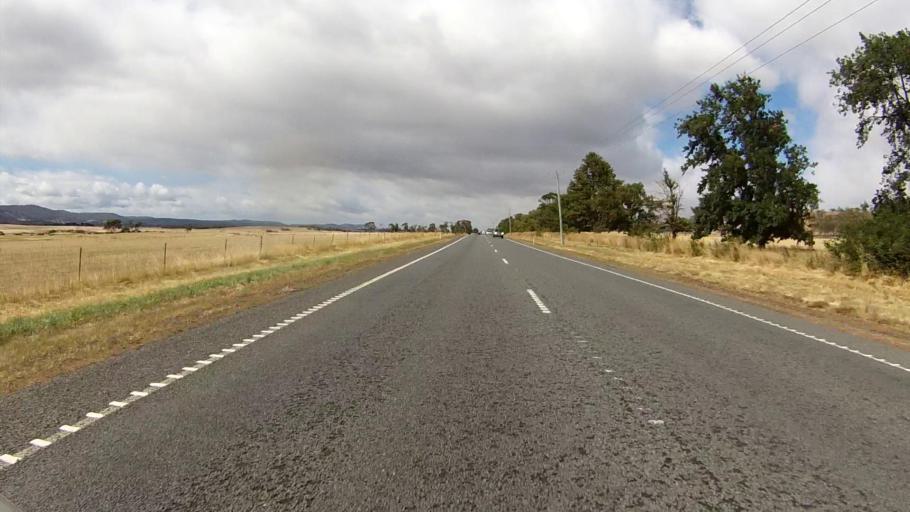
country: AU
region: Tasmania
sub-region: Northern Midlands
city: Evandale
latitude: -41.9698
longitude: 147.5014
